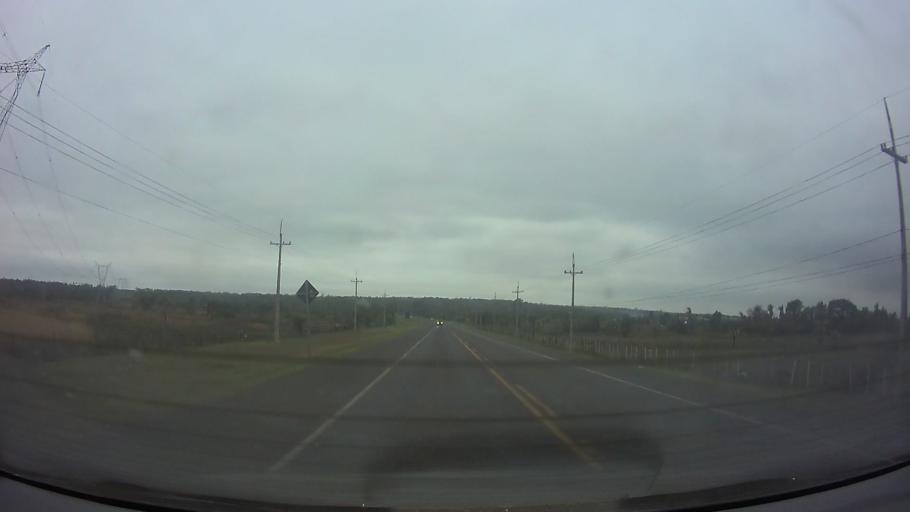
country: PY
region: Cordillera
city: Emboscada
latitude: -25.1091
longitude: -57.4127
